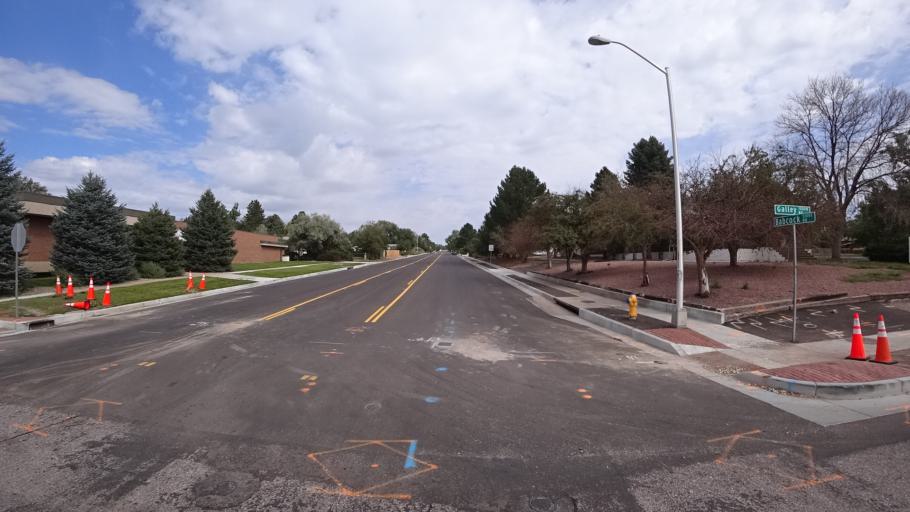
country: US
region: Colorado
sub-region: El Paso County
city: Cimarron Hills
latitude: 38.8467
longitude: -104.7295
